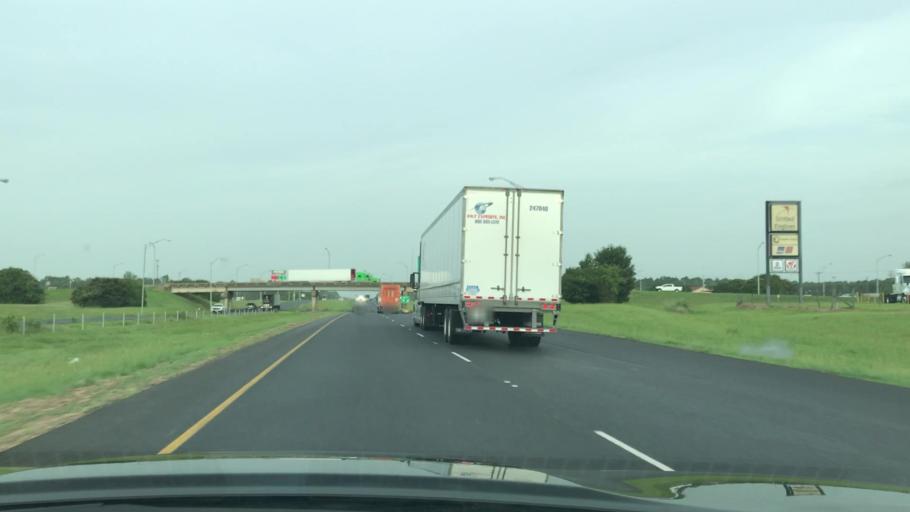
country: US
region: Louisiana
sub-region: Caddo Parish
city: Greenwood
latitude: 32.4477
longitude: -93.8970
